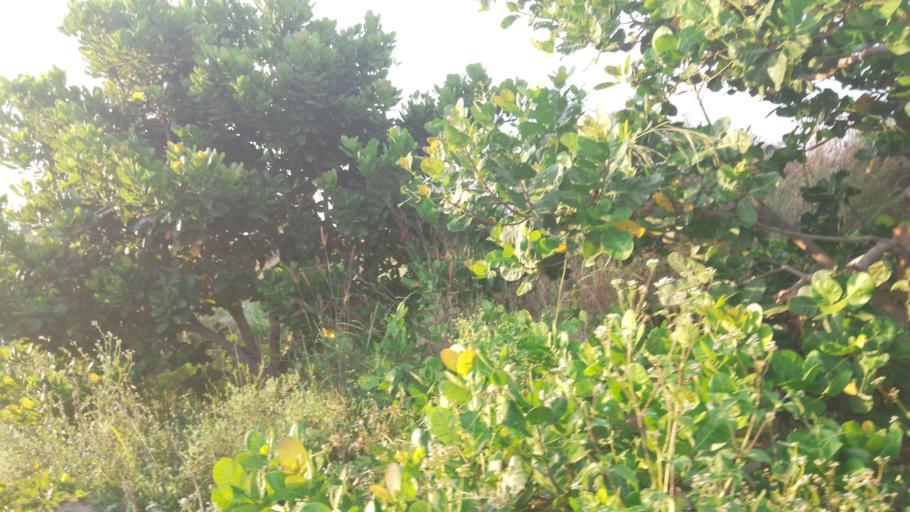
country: TG
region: Kara
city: Bafilo
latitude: 9.3936
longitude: 1.1463
